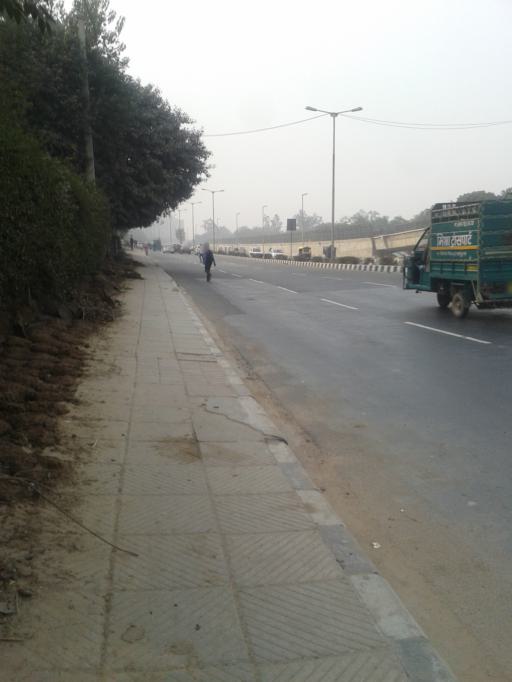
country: IN
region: NCT
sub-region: West Delhi
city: Nangloi Jat
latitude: 28.5796
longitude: 77.1011
